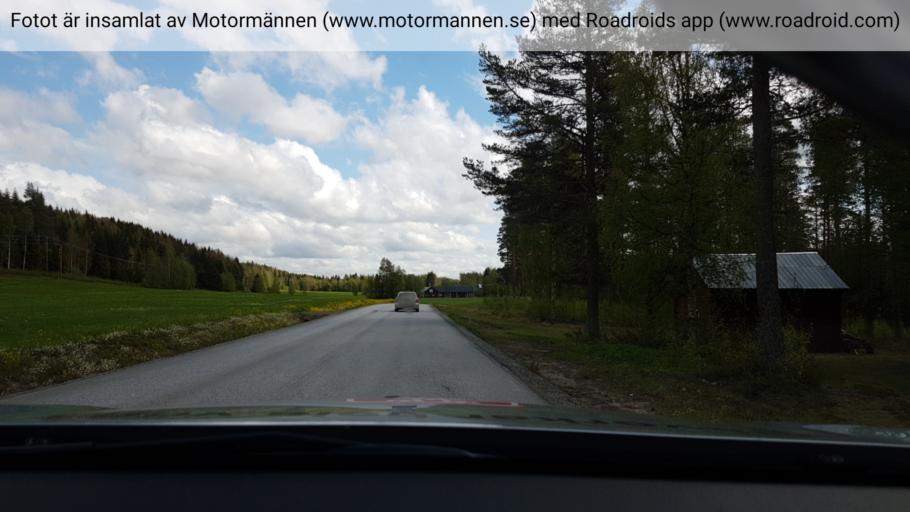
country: SE
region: Vaesterbotten
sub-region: Vindelns Kommun
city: Vindeln
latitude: 64.1800
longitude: 19.7190
